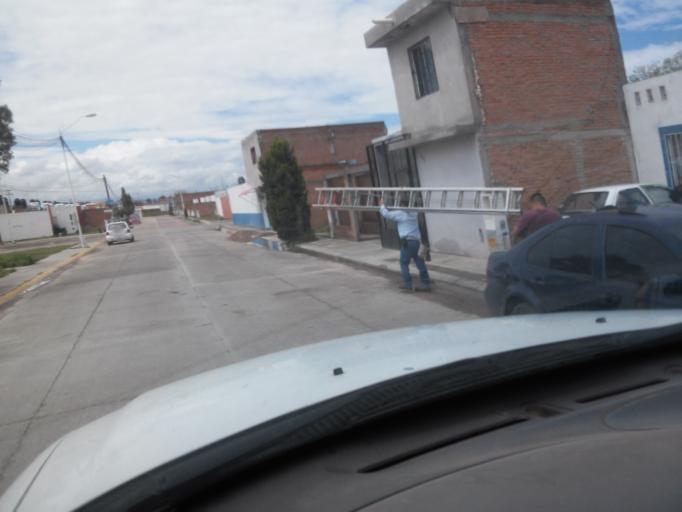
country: MX
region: Durango
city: Victoria de Durango
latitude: 24.0201
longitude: -104.6111
